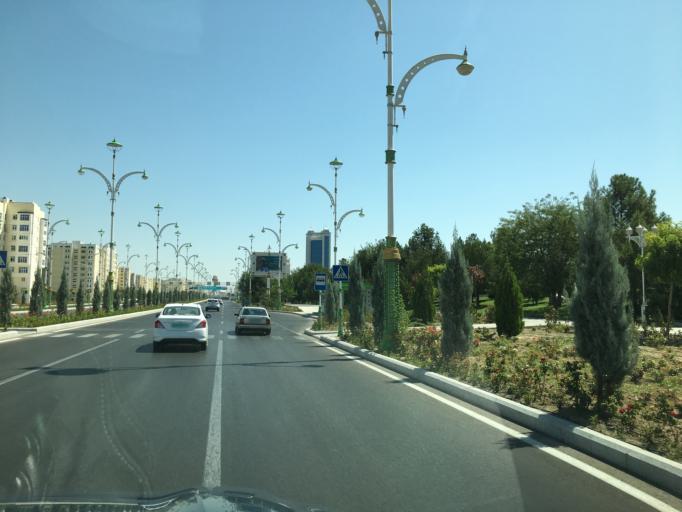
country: TM
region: Ahal
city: Ashgabat
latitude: 37.8955
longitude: 58.3810
